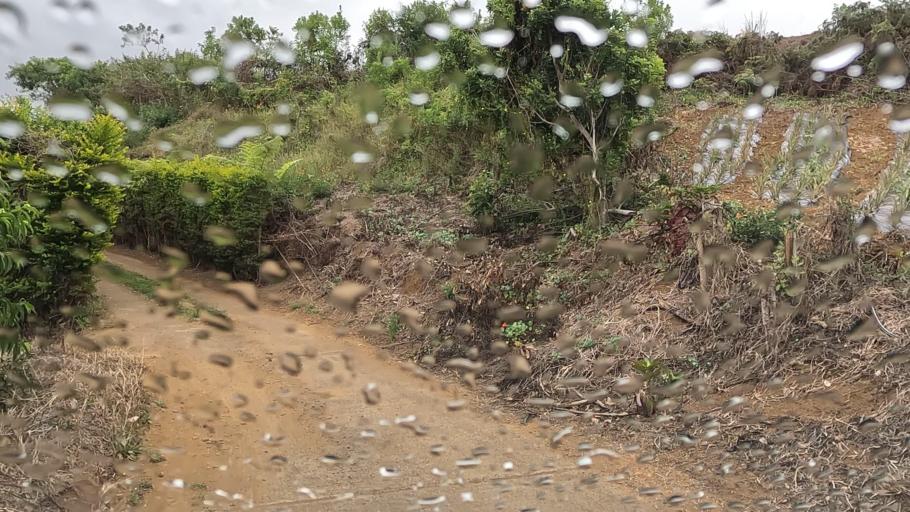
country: RE
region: Reunion
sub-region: Reunion
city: Le Tampon
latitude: -21.2913
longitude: 55.5487
